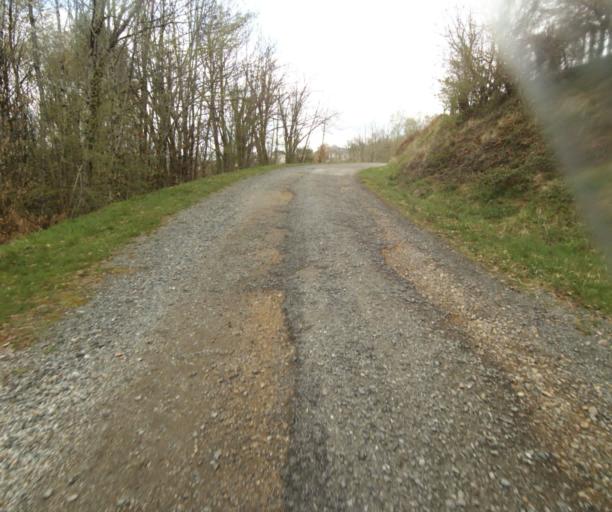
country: FR
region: Limousin
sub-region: Departement de la Correze
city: Tulle
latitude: 45.2899
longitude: 1.8018
